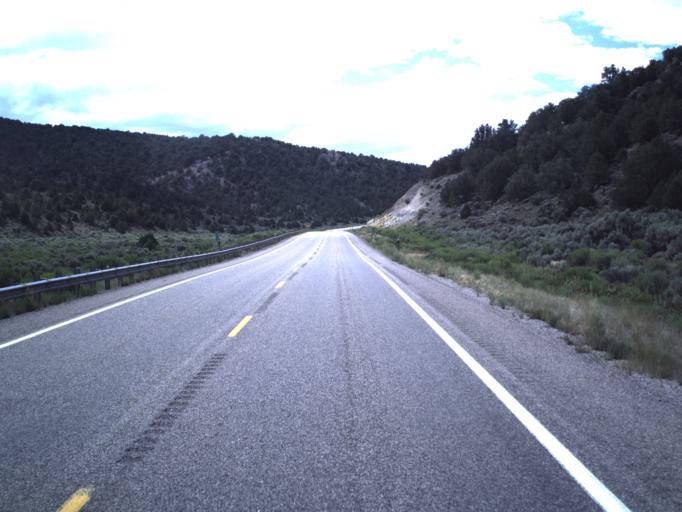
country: US
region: Utah
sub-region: Garfield County
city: Panguitch
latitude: 37.9873
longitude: -112.4942
